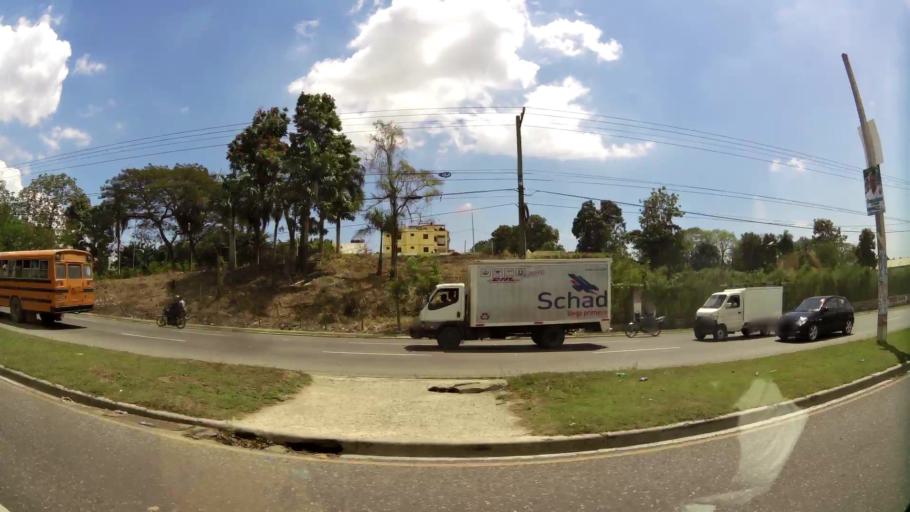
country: DO
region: Nacional
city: Ensanche Luperon
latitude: 18.5483
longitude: -69.8877
